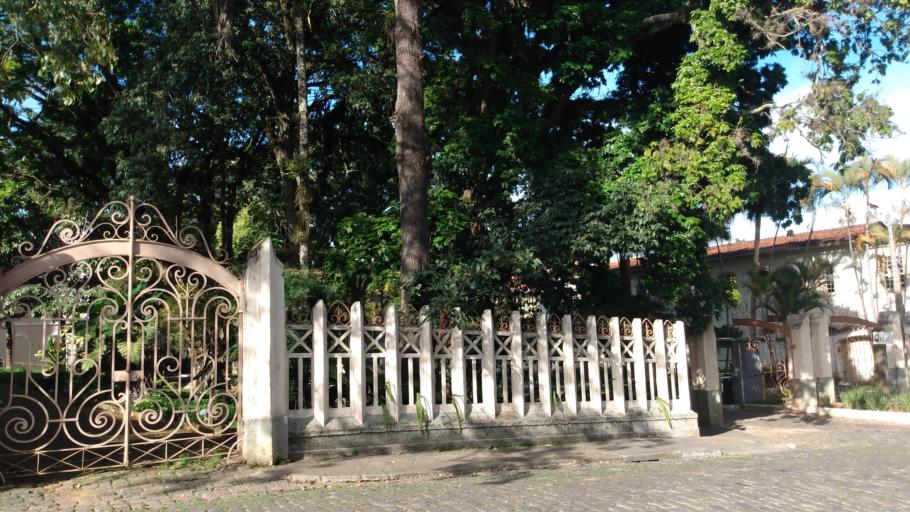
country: BR
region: Minas Gerais
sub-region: Sao Joao Del Rei
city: Sao Joao del Rei
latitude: -21.1392
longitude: -44.2601
